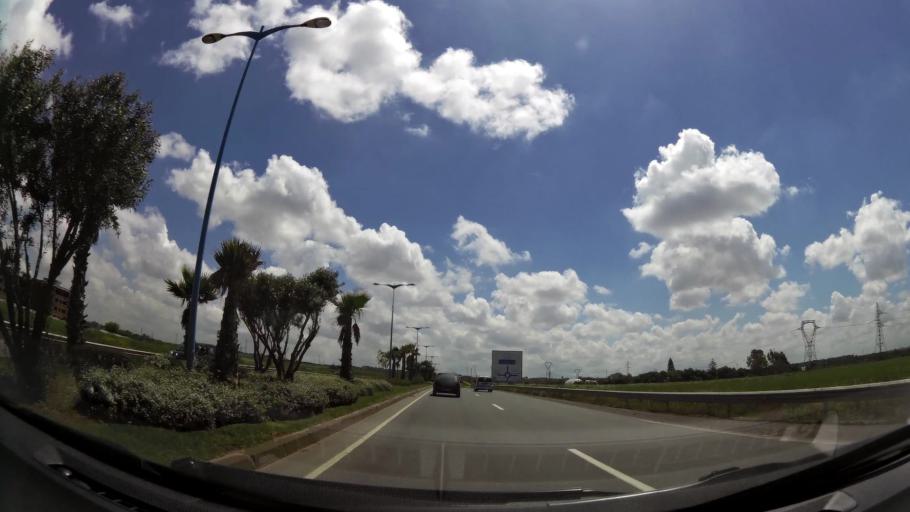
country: MA
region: Grand Casablanca
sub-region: Casablanca
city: Casablanca
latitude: 33.5196
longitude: -7.6158
